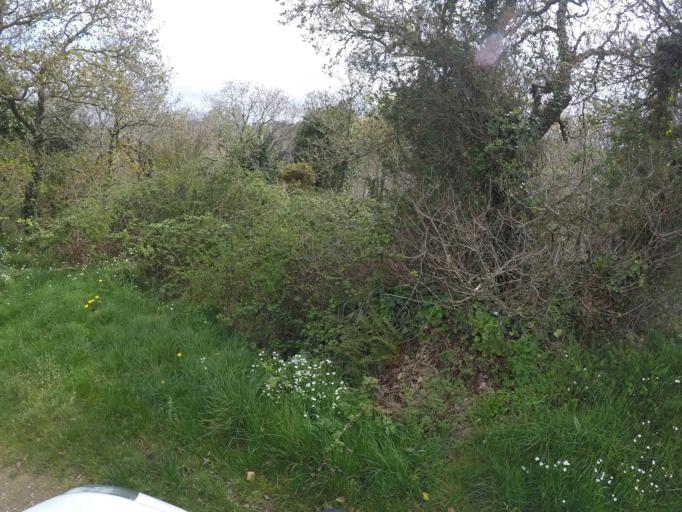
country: FR
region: Brittany
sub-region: Departement des Cotes-d'Armor
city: Plouha
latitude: 48.7187
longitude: -2.9440
